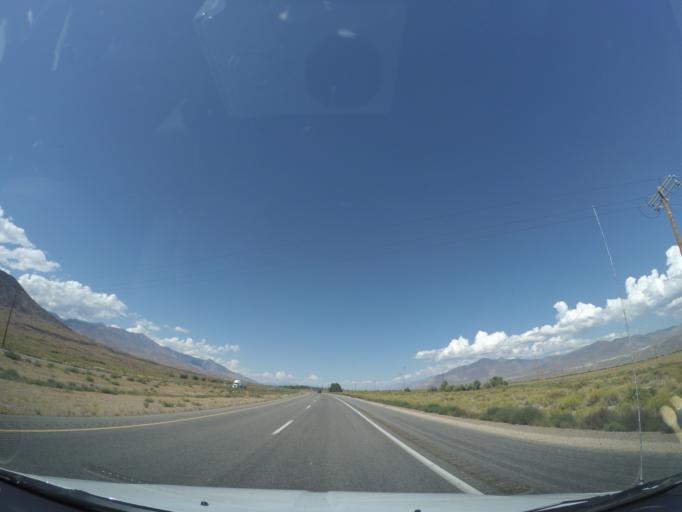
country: US
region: California
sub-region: Inyo County
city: Big Pine
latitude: 37.1081
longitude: -118.2536
